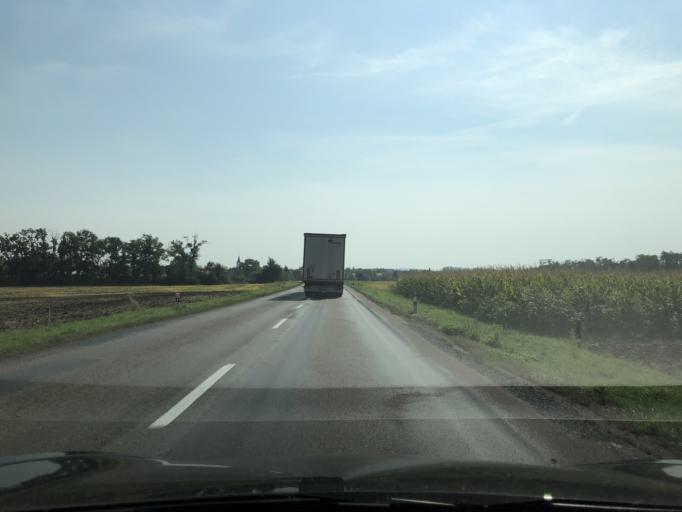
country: CZ
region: South Moravian
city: Novosedly
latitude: 48.8291
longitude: 16.5278
